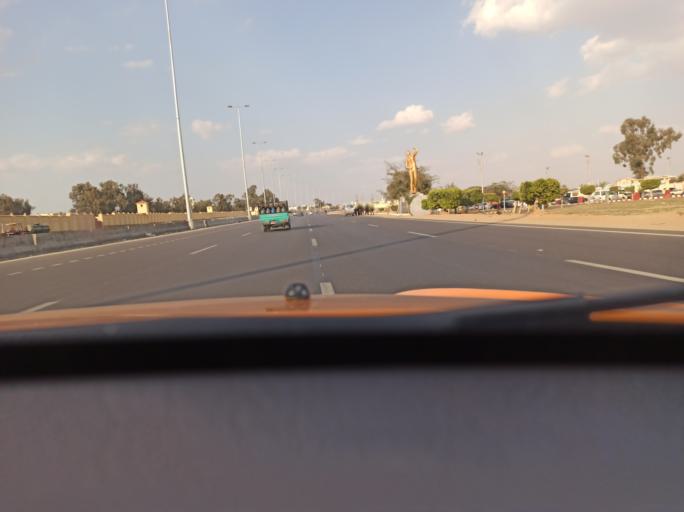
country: EG
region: Al Isma'iliyah
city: Ismailia
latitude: 30.6126
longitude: 32.2215
